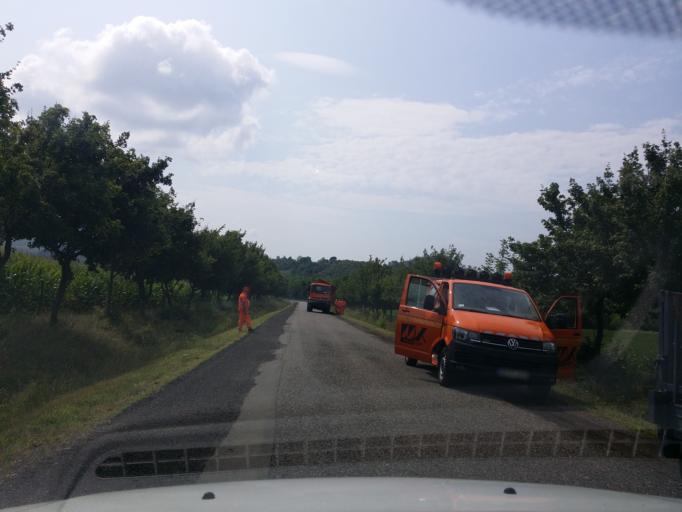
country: HU
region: Borsod-Abauj-Zemplen
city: Sarospatak
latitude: 48.4678
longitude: 21.5231
